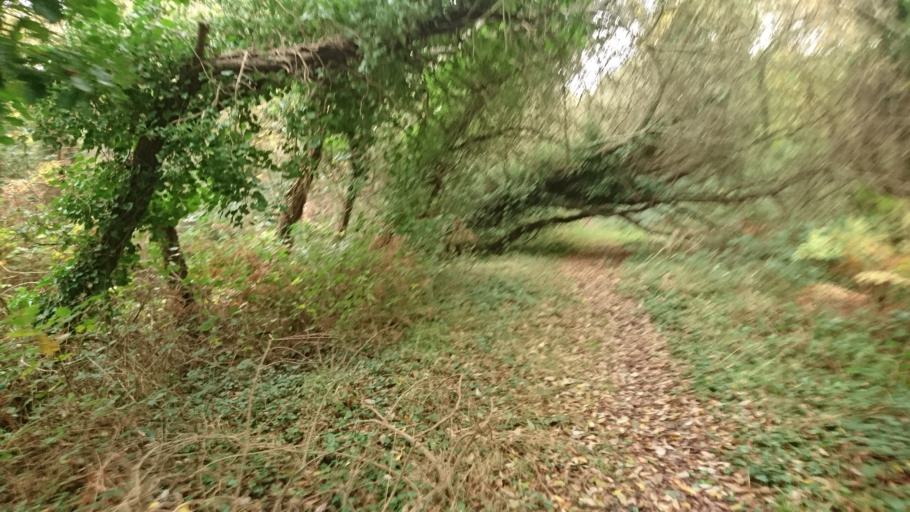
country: FR
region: Brittany
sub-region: Departement du Finistere
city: Lampaul-Plouarzel
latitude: 48.4370
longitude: -4.7687
